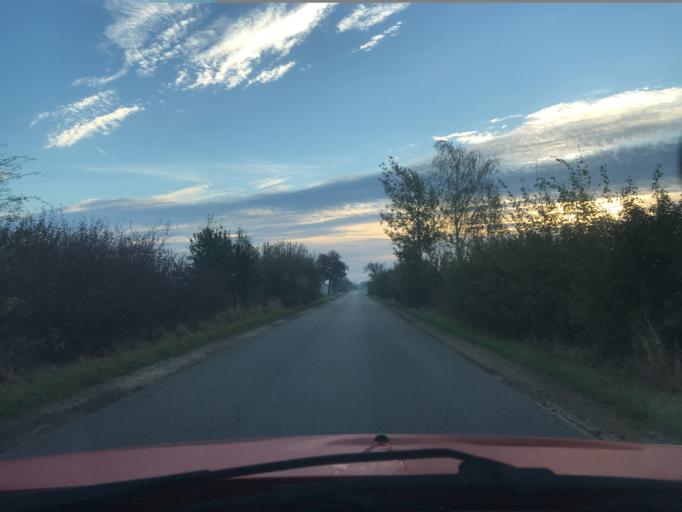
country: PL
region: Greater Poland Voivodeship
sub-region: Powiat ostrowski
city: Raszkow
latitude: 51.7190
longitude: 17.7720
